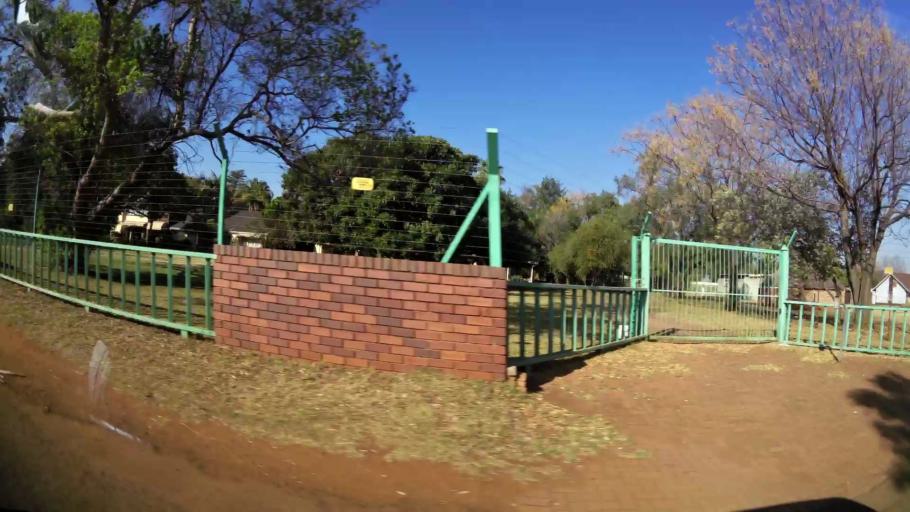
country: ZA
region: Gauteng
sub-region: City of Tshwane Metropolitan Municipality
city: Pretoria
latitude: -25.6480
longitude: 28.2196
